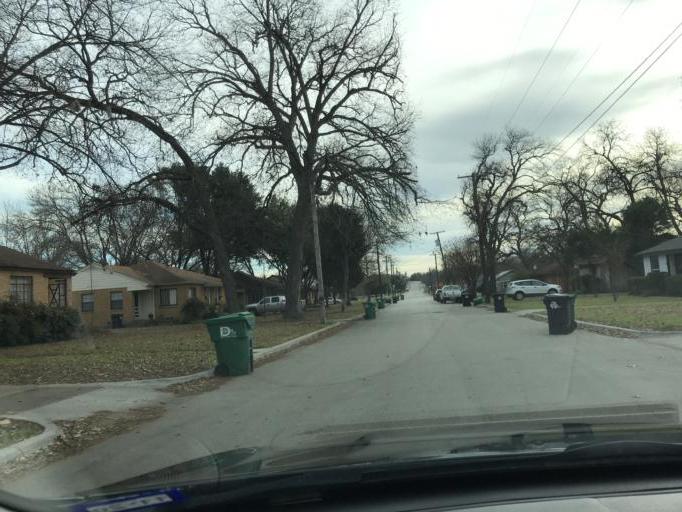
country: US
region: Texas
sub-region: Denton County
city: Denton
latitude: 33.2227
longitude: -97.1390
